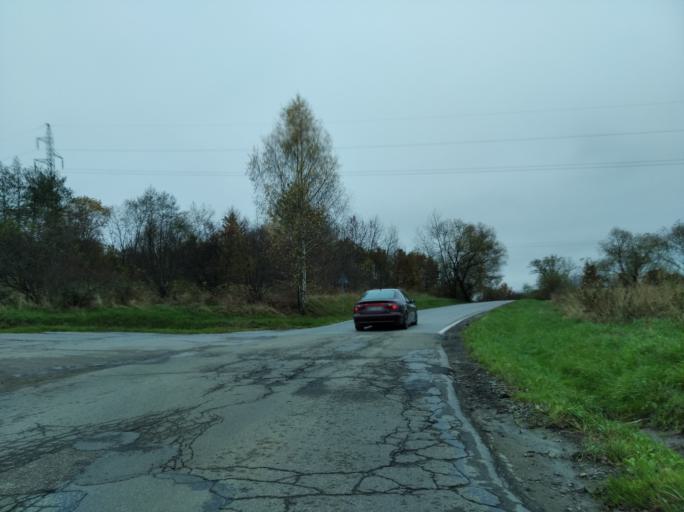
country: PL
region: Subcarpathian Voivodeship
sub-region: Krosno
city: Krosno
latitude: 49.7112
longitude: 21.7585
